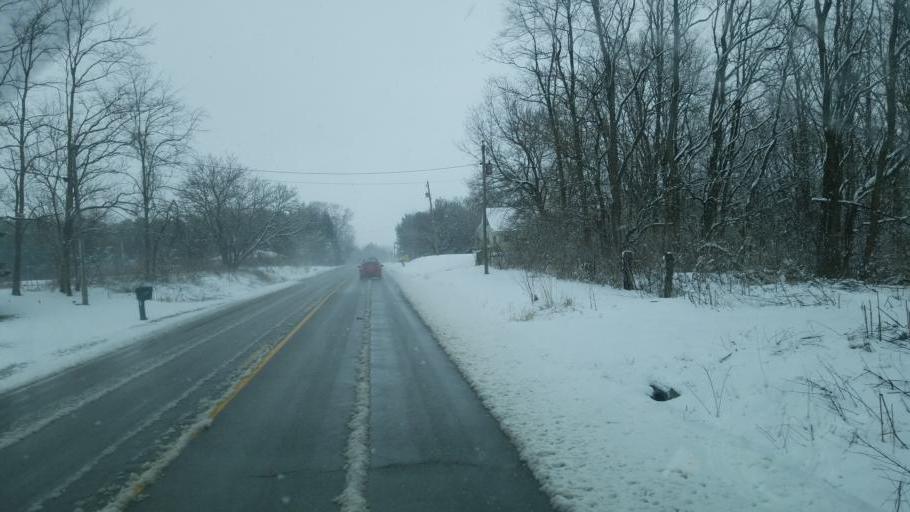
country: US
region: Indiana
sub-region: Delaware County
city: Muncie
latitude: 40.0885
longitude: -85.3011
